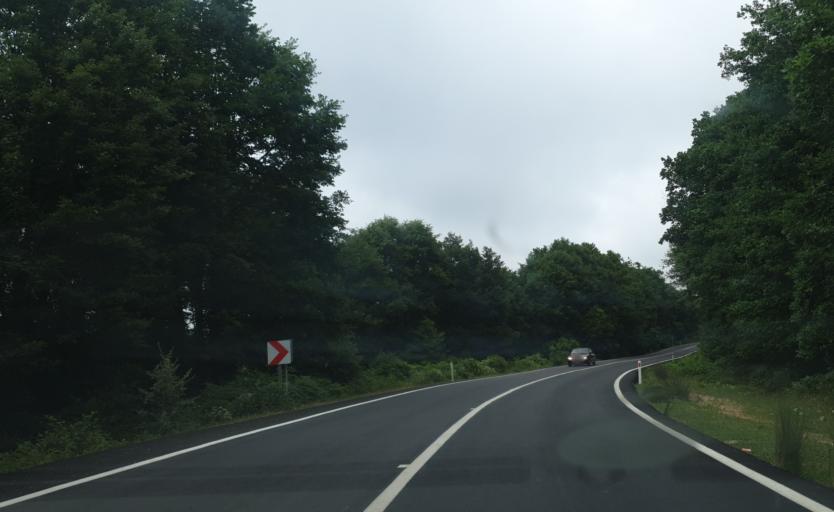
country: TR
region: Kirklareli
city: Salmydessus
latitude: 41.5912
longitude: 28.0735
